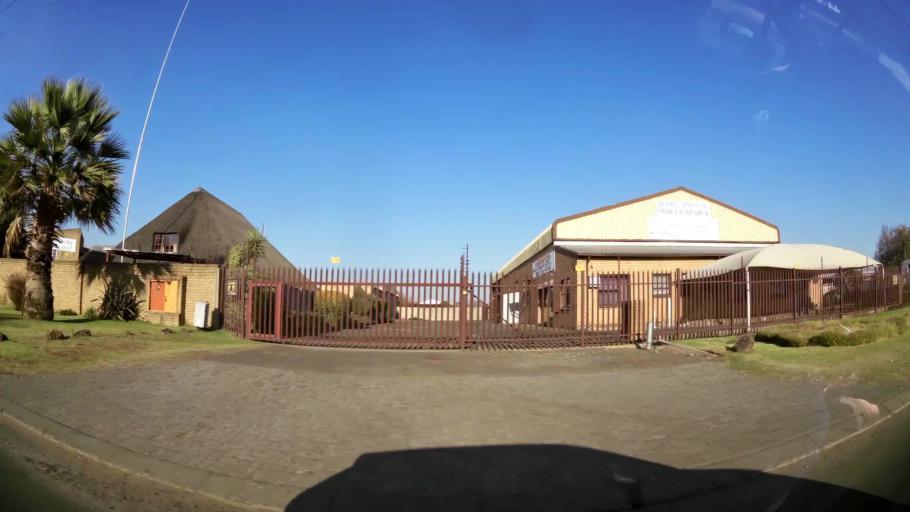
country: ZA
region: Gauteng
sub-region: West Rand District Municipality
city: Randfontein
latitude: -26.1926
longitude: 27.6927
